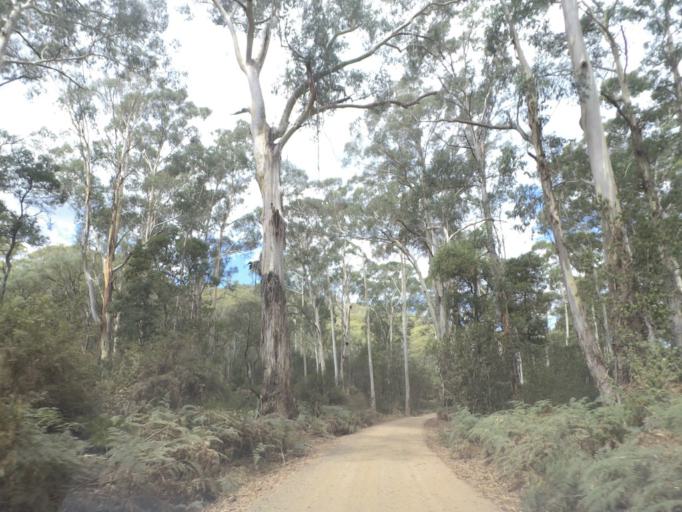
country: AU
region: Victoria
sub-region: Murrindindi
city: Alexandra
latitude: -37.3603
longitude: 145.7541
